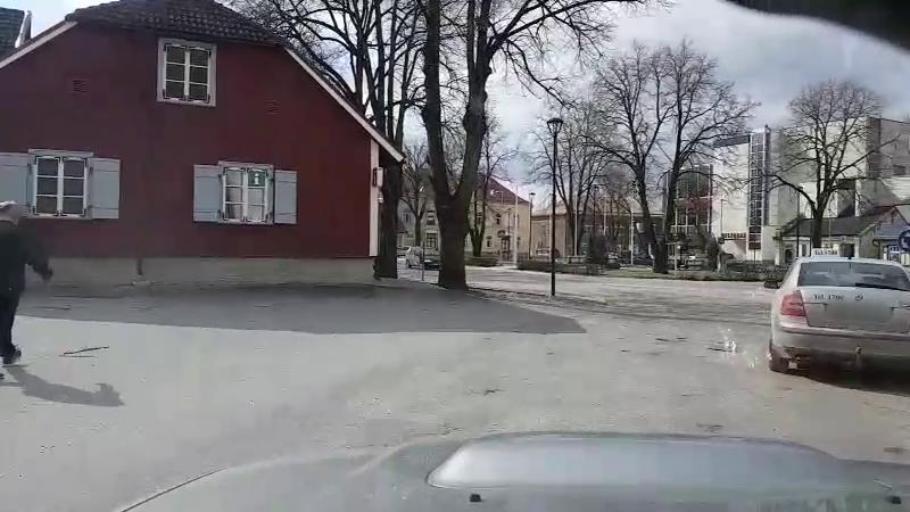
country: EE
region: Jaervamaa
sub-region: Paide linn
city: Paide
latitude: 58.8875
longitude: 25.5706
